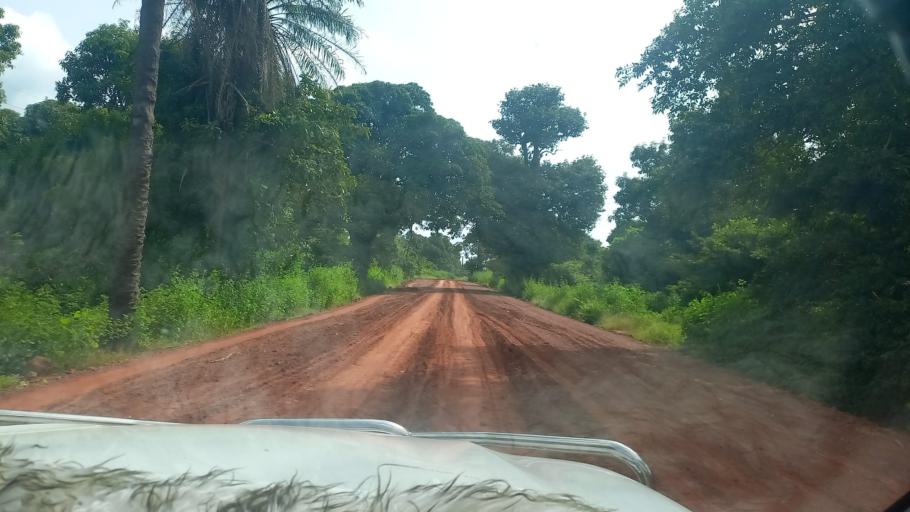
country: SN
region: Ziguinchor
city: Bignona
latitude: 12.7555
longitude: -16.2714
